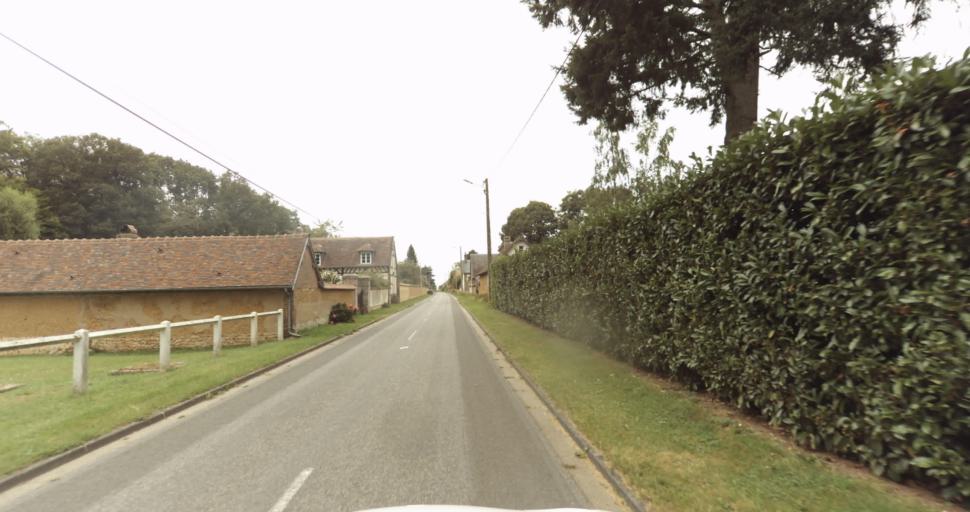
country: FR
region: Haute-Normandie
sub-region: Departement de l'Eure
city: Arnieres-sur-Iton
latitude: 48.9416
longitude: 1.0769
